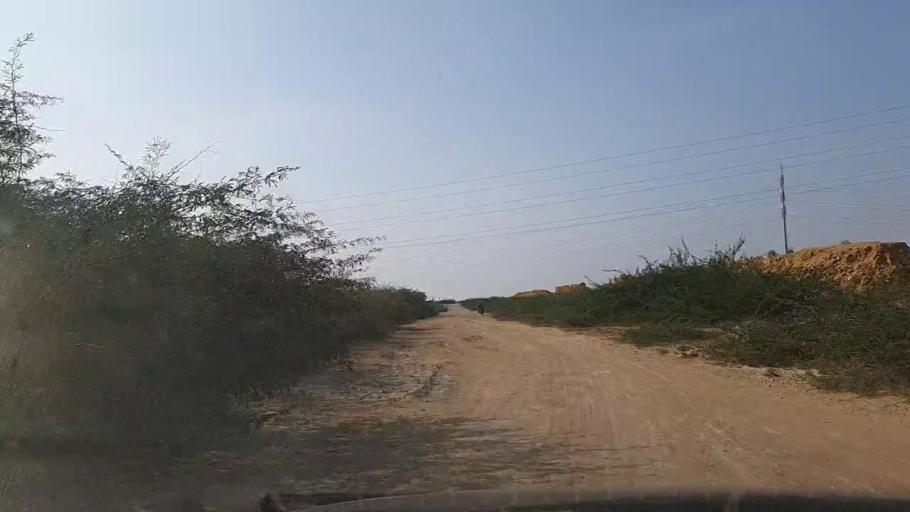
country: PK
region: Sindh
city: Gharo
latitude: 24.7527
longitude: 67.5409
